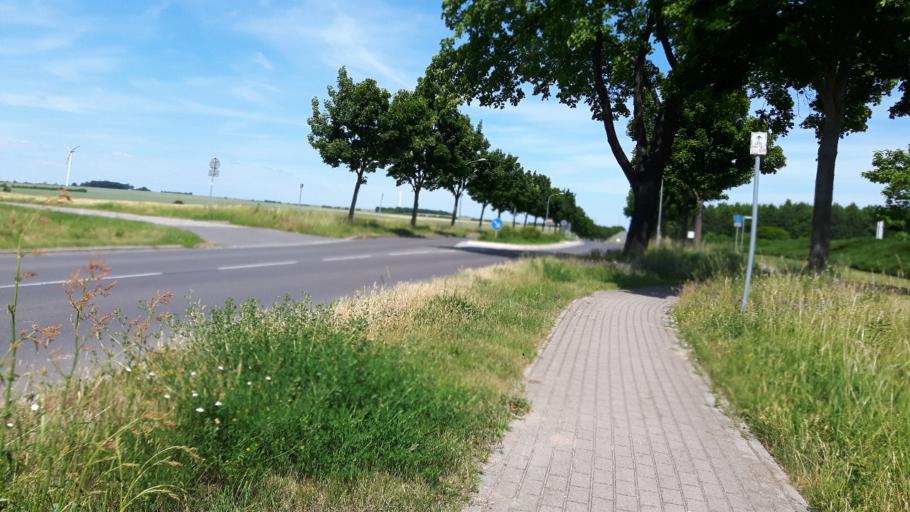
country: DE
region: Saxony-Anhalt
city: Kropstadt
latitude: 52.0039
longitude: 12.7815
